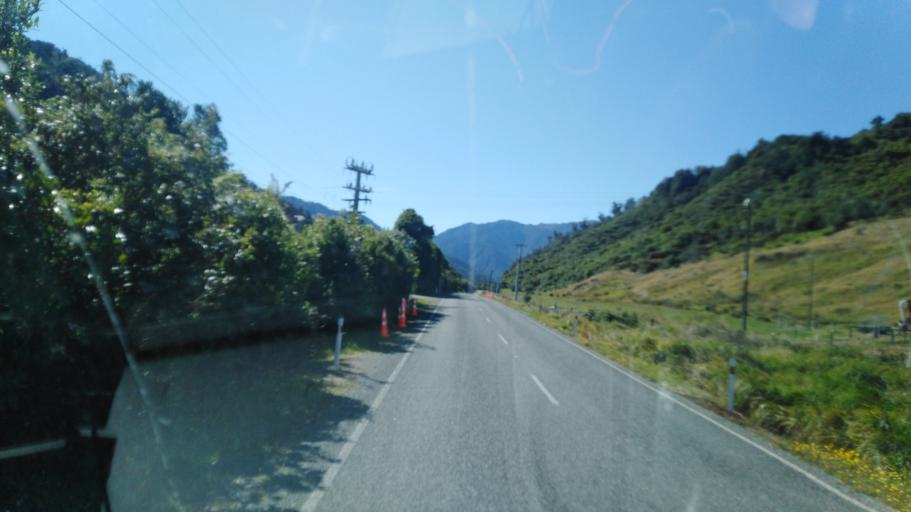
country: NZ
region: West Coast
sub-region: Buller District
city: Westport
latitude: -41.5291
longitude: 171.9451
